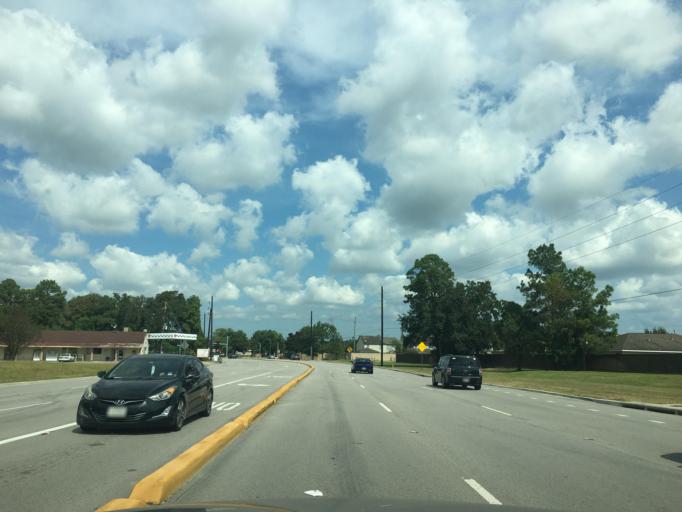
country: US
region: Texas
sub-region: Harris County
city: Spring
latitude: 30.1180
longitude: -95.3971
